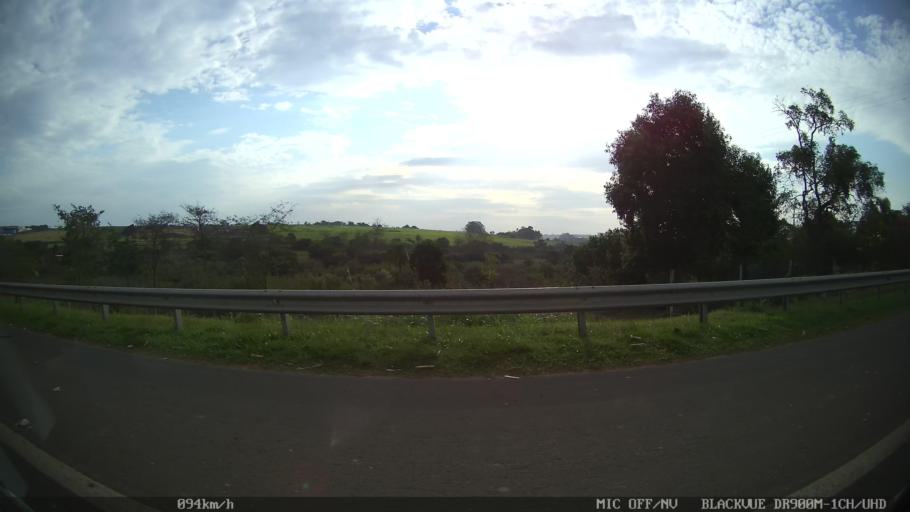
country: BR
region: Sao Paulo
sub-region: Cosmopolis
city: Cosmopolis
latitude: -22.6121
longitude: -47.1954
